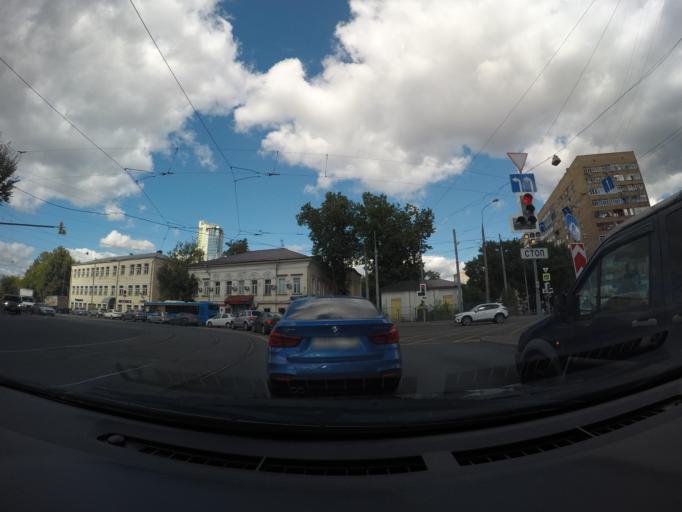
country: RU
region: Moscow
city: Lefortovo
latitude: 55.7796
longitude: 37.7208
